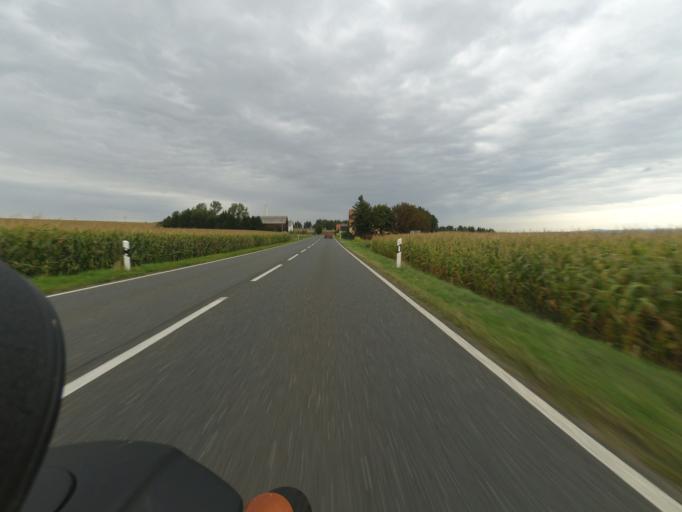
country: DE
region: Saxony
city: Hermsdorf
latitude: 50.9491
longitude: 13.7000
